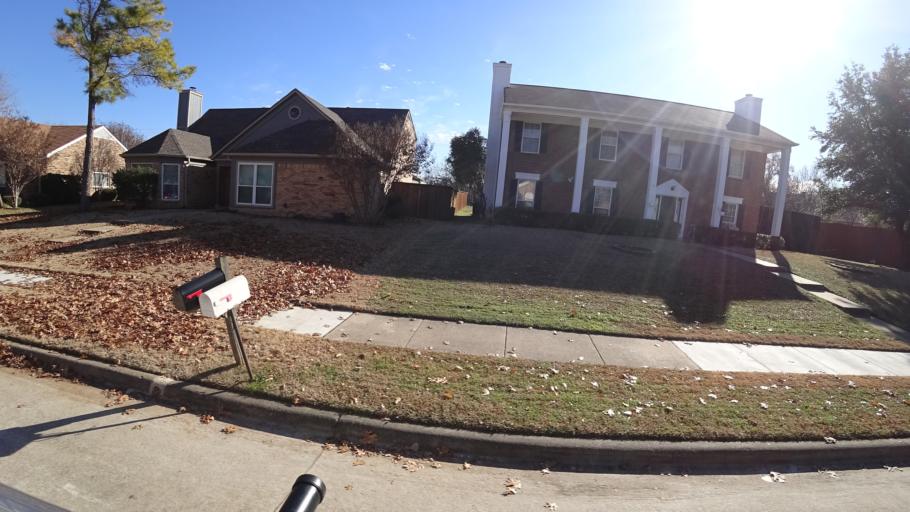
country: US
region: Texas
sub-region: Denton County
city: Lewisville
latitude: 33.0188
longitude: -97.0291
